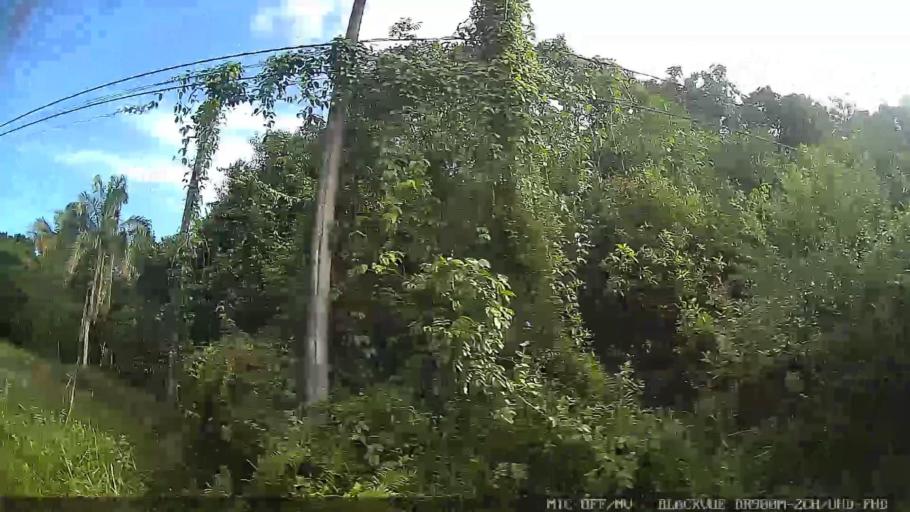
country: BR
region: Sao Paulo
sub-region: Itanhaem
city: Itanhaem
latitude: -24.1968
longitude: -46.8966
